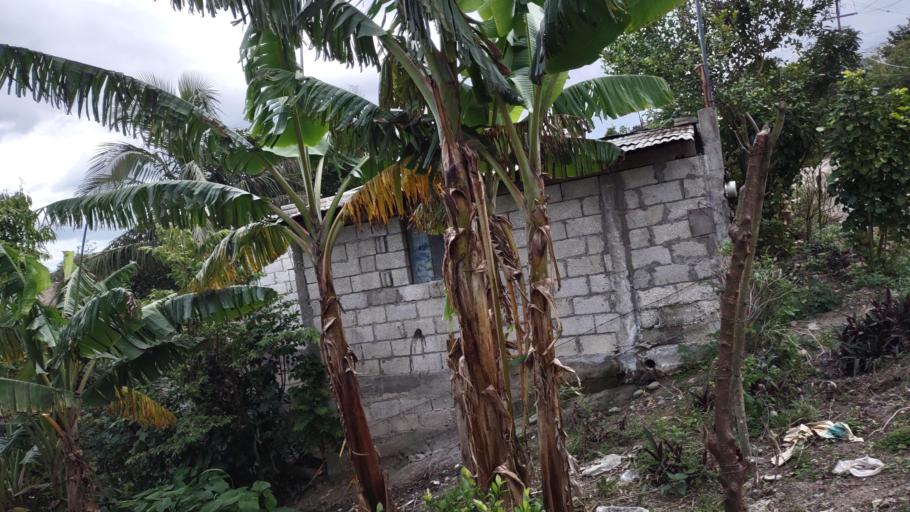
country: MX
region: Veracruz
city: Papantla de Olarte
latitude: 20.4320
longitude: -97.3396
